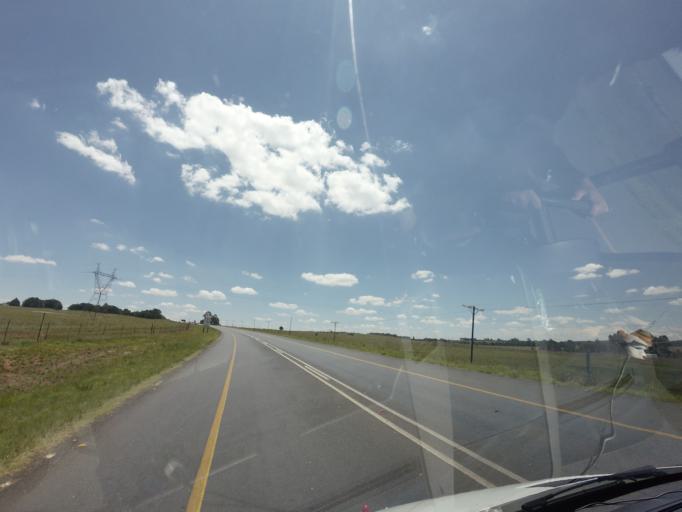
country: ZA
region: Mpumalanga
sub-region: Nkangala District Municipality
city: Belfast
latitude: -25.7145
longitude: 30.0720
